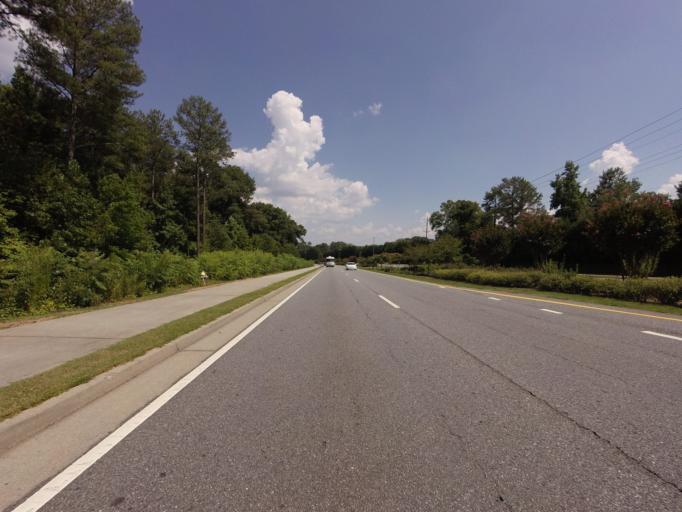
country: US
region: Georgia
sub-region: Fulton County
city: Johns Creek
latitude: 34.0325
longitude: -84.2108
